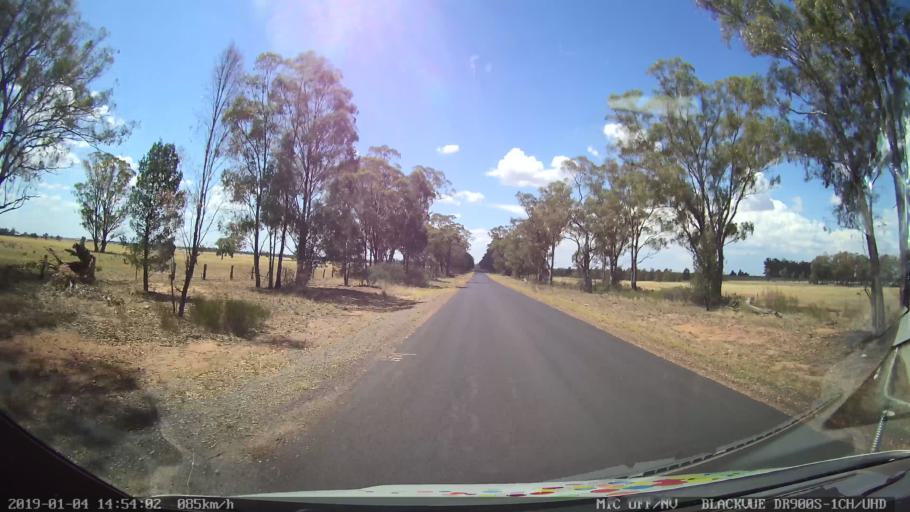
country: AU
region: New South Wales
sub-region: Dubbo Municipality
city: Dubbo
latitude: -31.9959
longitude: 148.6531
